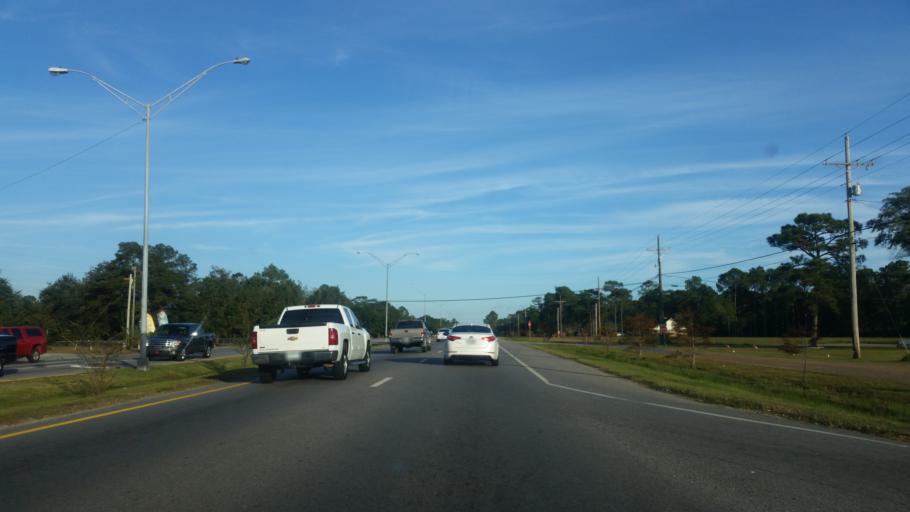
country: US
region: Mississippi
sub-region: Jackson County
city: Gulf Park Estates
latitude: 30.4086
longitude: -88.7575
